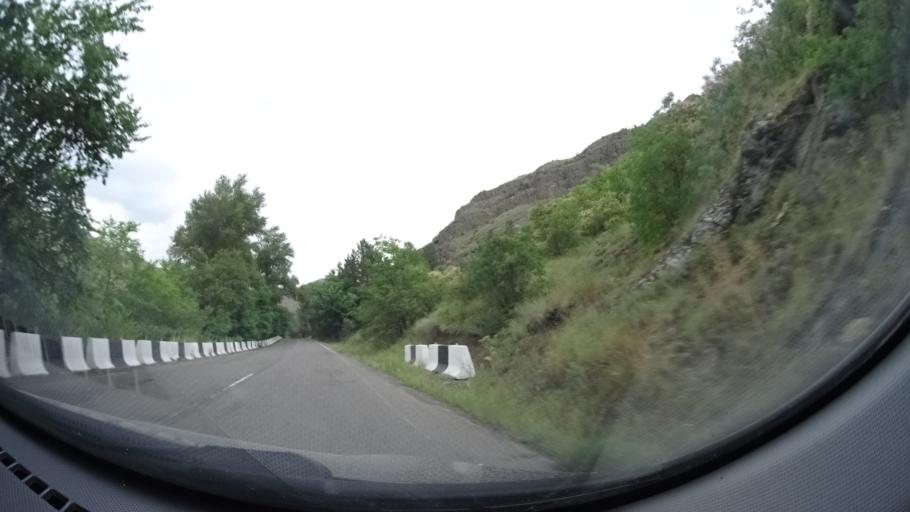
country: GE
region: Samtskhe-Javakheti
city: Akhaltsikhe
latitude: 41.6133
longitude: 43.0648
